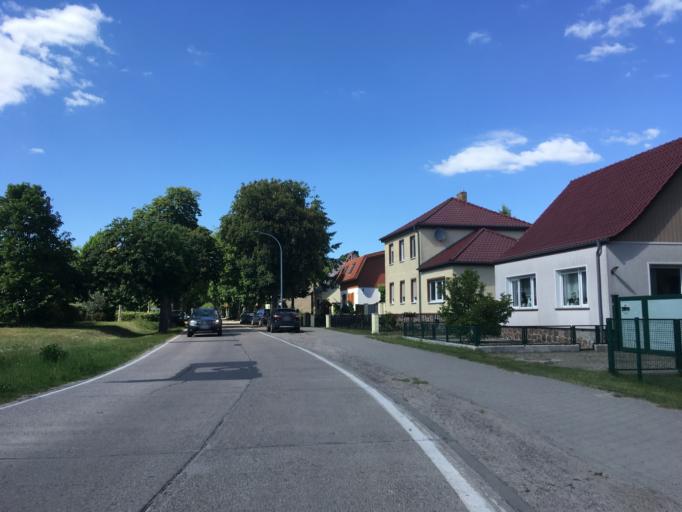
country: DE
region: Brandenburg
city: Joachimsthal
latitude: 52.9868
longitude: 13.7438
